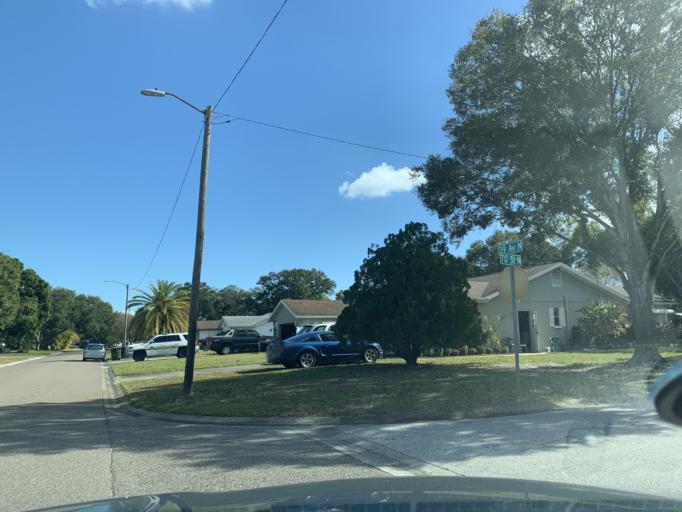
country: US
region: Florida
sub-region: Pinellas County
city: Kenneth City
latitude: 27.8072
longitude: -82.7356
